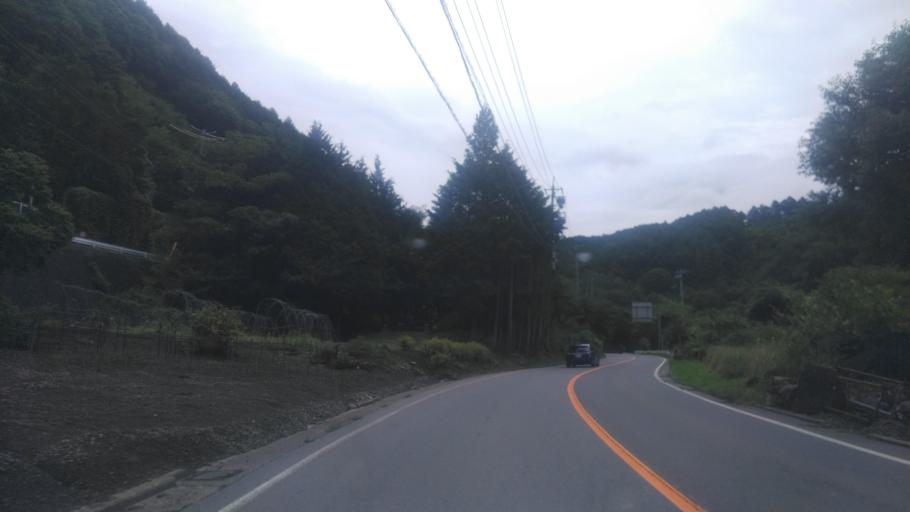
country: JP
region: Nagano
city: Ueda
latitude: 36.4911
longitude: 138.3604
